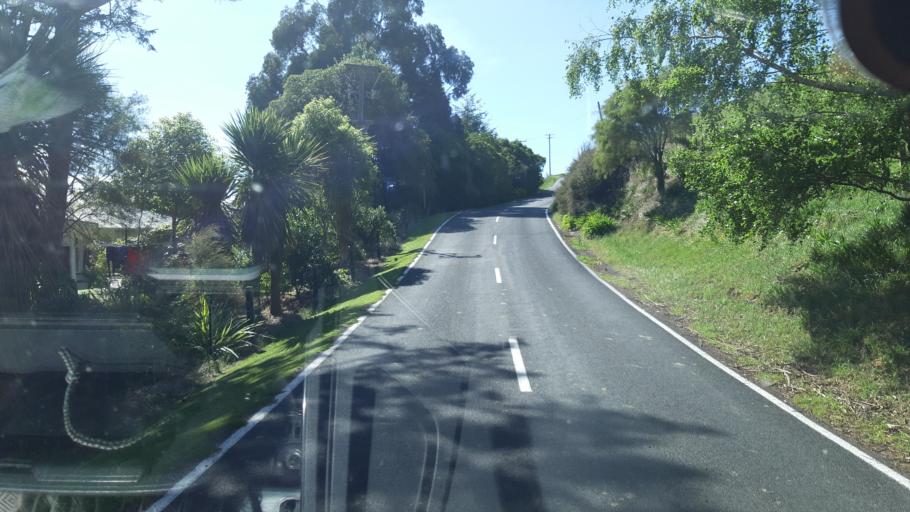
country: NZ
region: Otago
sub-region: Dunedin City
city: Portobello
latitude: -45.6587
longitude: 170.6430
